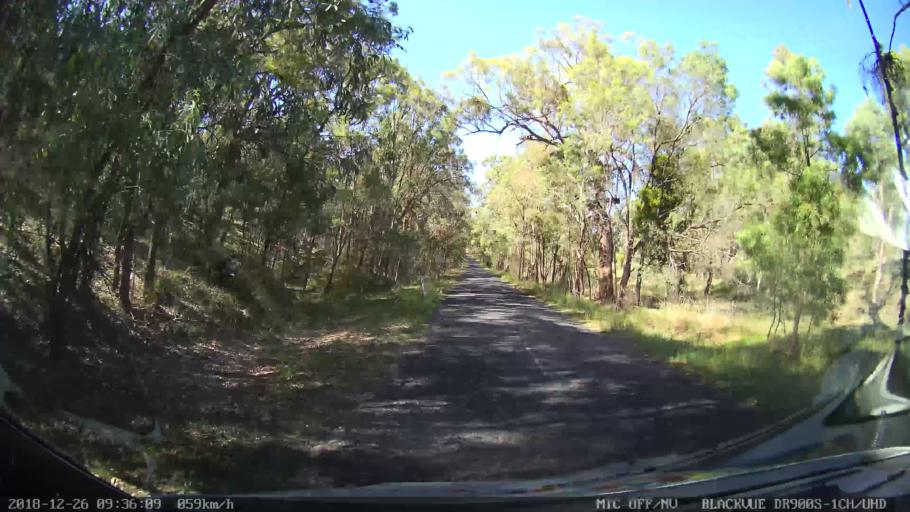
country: AU
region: New South Wales
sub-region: Mid-Western Regional
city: Kandos
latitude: -32.9214
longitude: 150.0406
